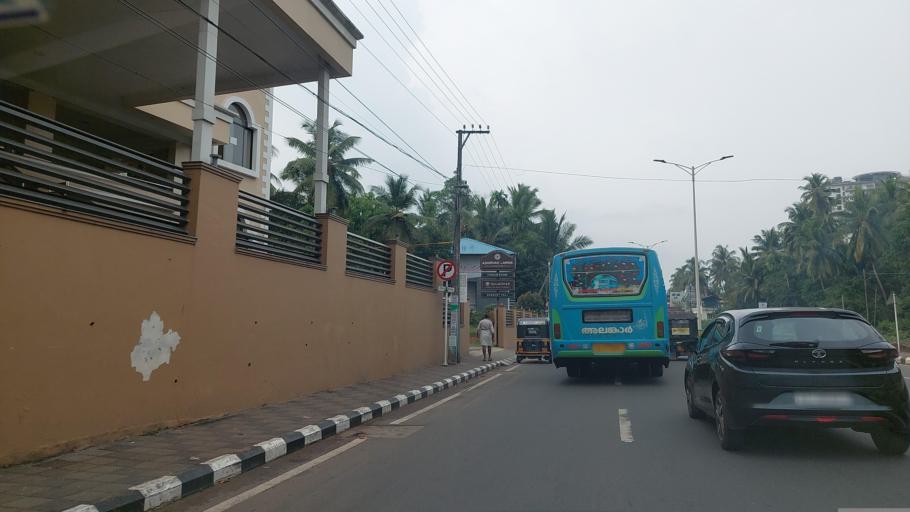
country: IN
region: Kerala
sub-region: Kozhikode
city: Kozhikode
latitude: 11.2834
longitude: 75.7834
